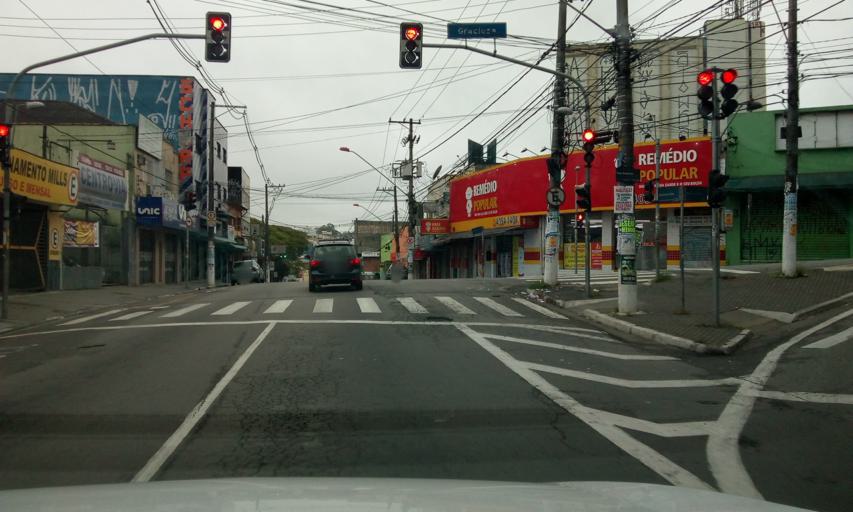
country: BR
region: Sao Paulo
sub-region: Diadema
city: Diadema
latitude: -23.6883
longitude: -46.6253
